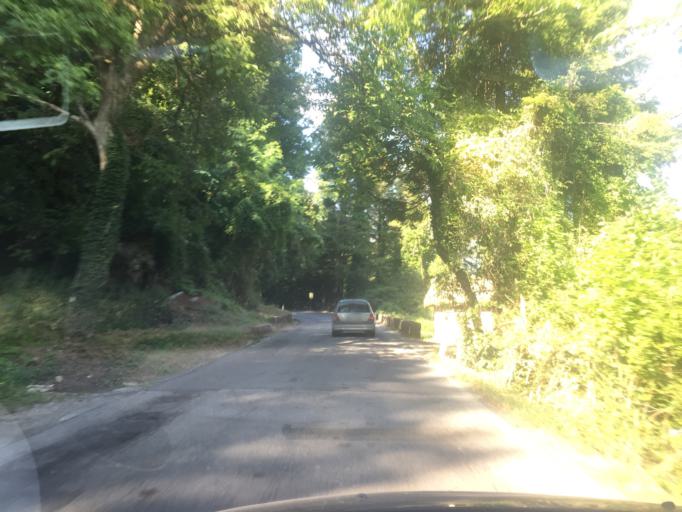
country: IT
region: Tuscany
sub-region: Provincia di Lucca
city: Camporgiano
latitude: 44.1411
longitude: 10.3471
